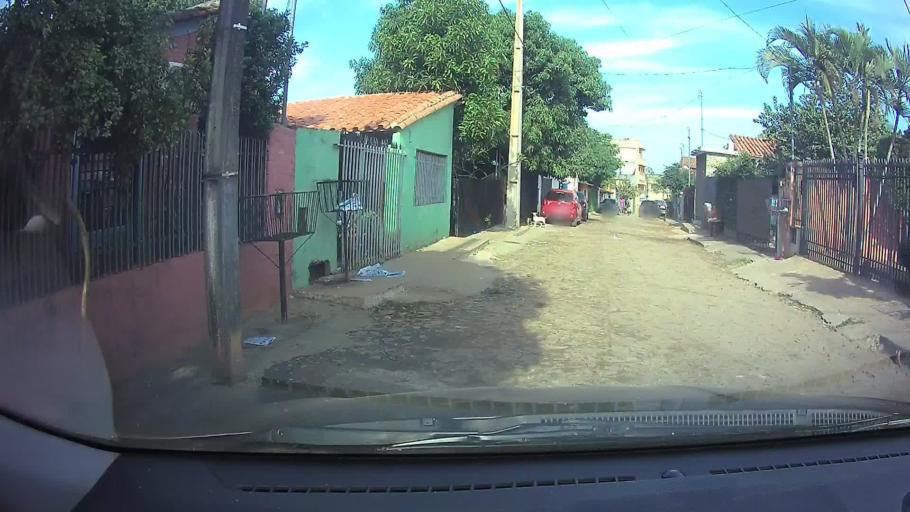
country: PY
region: Central
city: Villa Elisa
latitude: -25.3540
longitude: -57.5703
